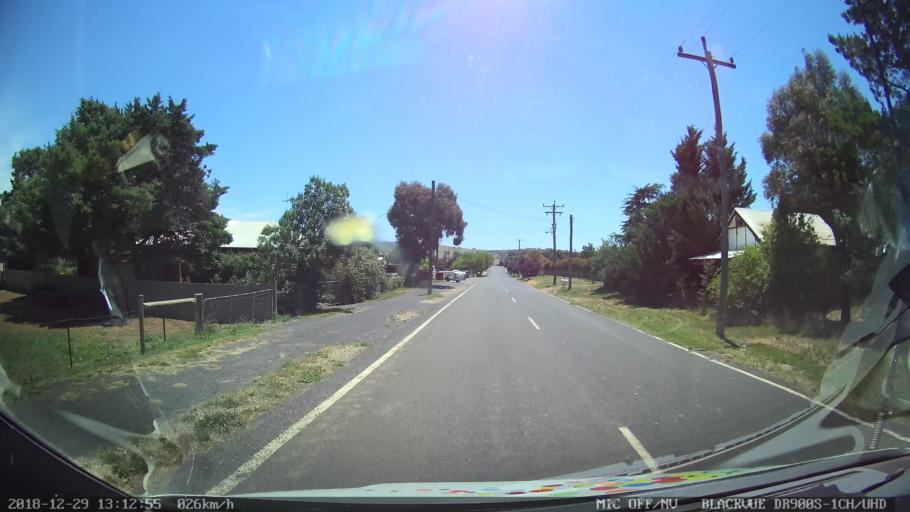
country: AU
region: Australian Capital Territory
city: Macarthur
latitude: -35.7090
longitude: 149.1648
